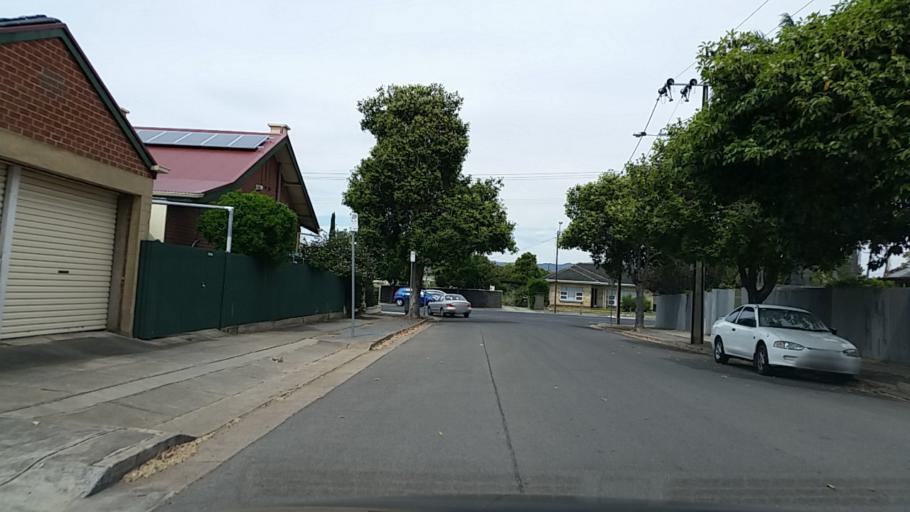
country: AU
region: South Australia
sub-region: City of West Torrens
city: Plympton
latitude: -34.9537
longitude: 138.5534
